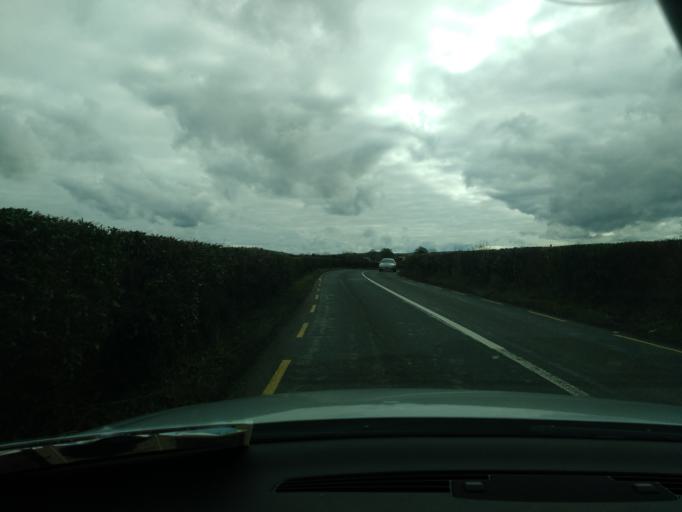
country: IE
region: Leinster
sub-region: Laois
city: Rathdowney
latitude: 52.7216
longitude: -7.5383
